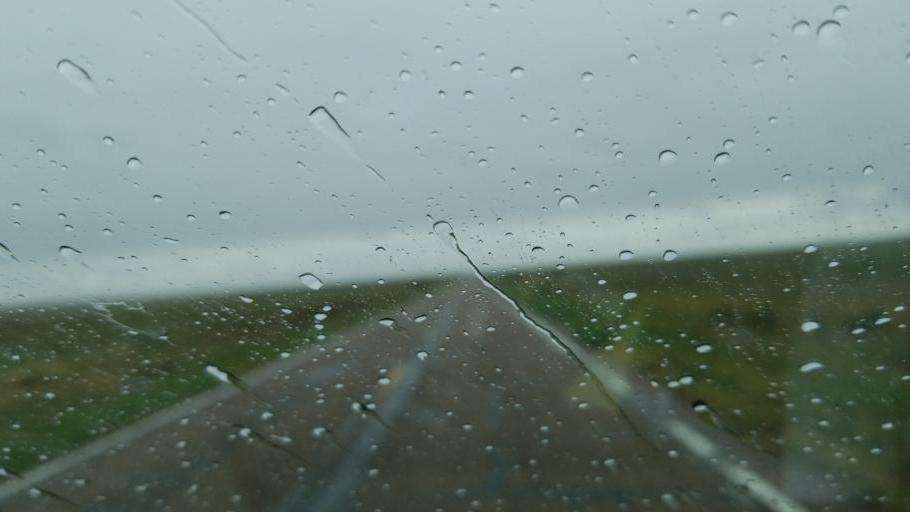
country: US
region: Colorado
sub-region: Lincoln County
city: Hugo
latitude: 38.8497
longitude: -103.1872
